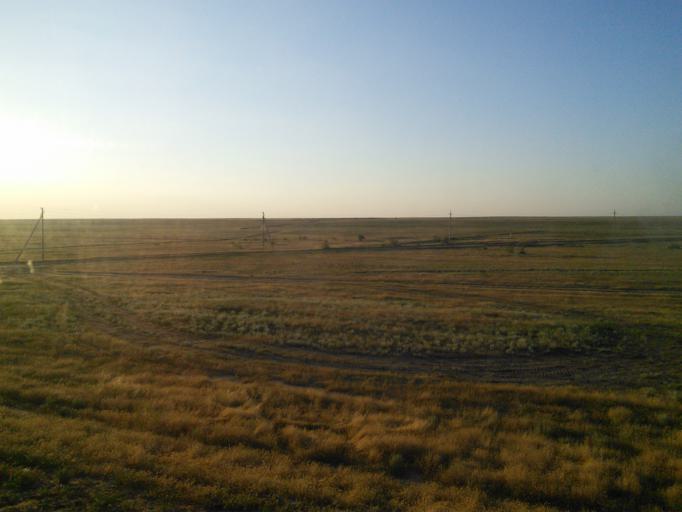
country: RU
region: Astrakhan
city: Zenzeli
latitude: 46.2747
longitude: 47.2570
